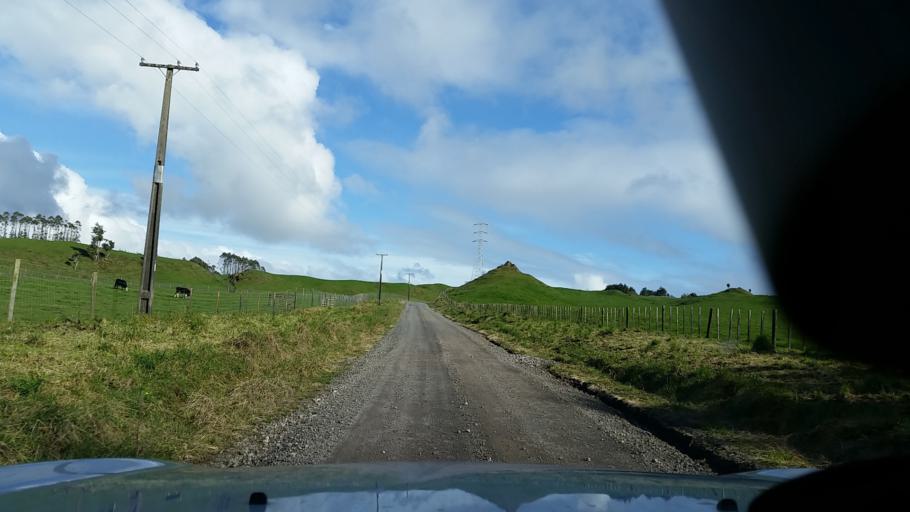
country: NZ
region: Bay of Plenty
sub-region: Rotorua District
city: Rotorua
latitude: -38.0048
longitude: 176.2023
